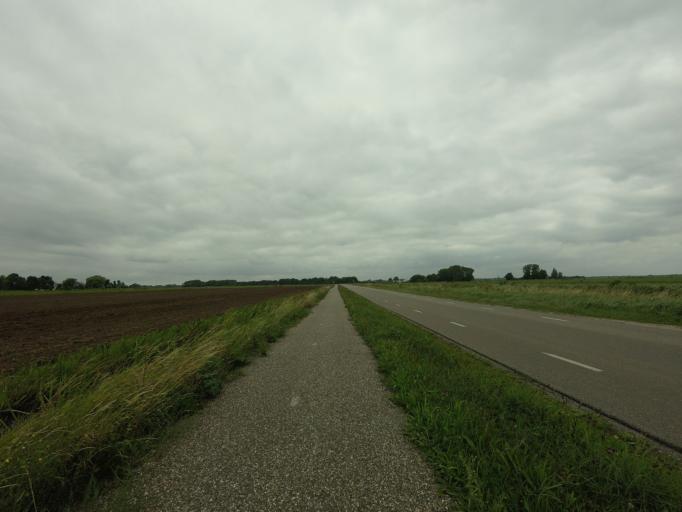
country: NL
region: Utrecht
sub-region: Stichtse Vecht
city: Breukelen
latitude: 52.1820
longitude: 4.9345
